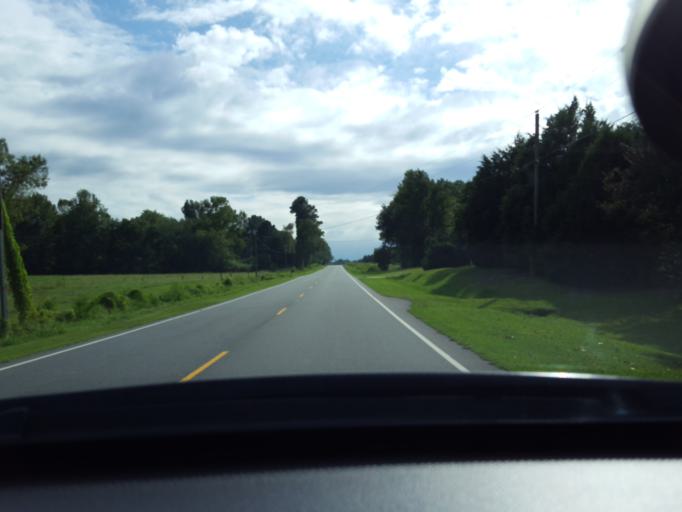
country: US
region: North Carolina
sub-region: Duplin County
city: Kenansville
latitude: 35.0007
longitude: -77.9166
